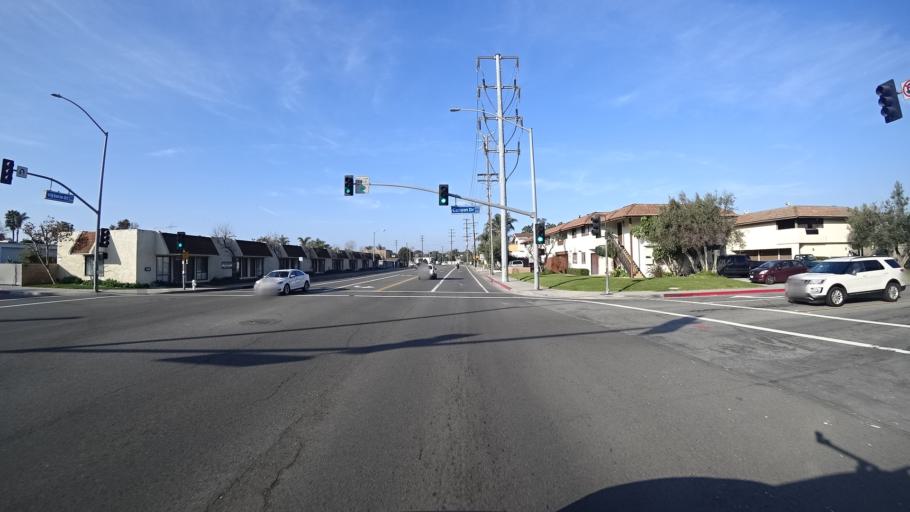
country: US
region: California
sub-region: Orange County
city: Costa Mesa
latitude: 33.6524
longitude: -117.9439
